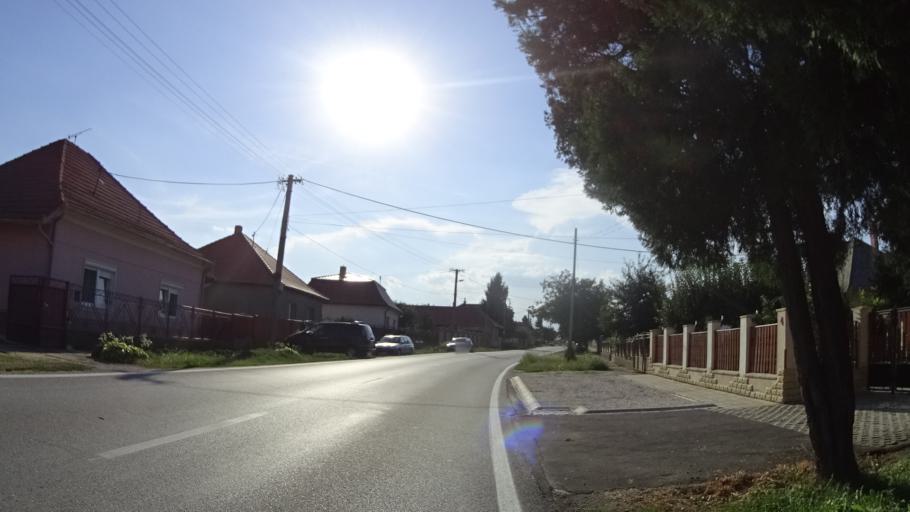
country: HU
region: Komarom-Esztergom
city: Tat
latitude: 47.7900
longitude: 18.6114
